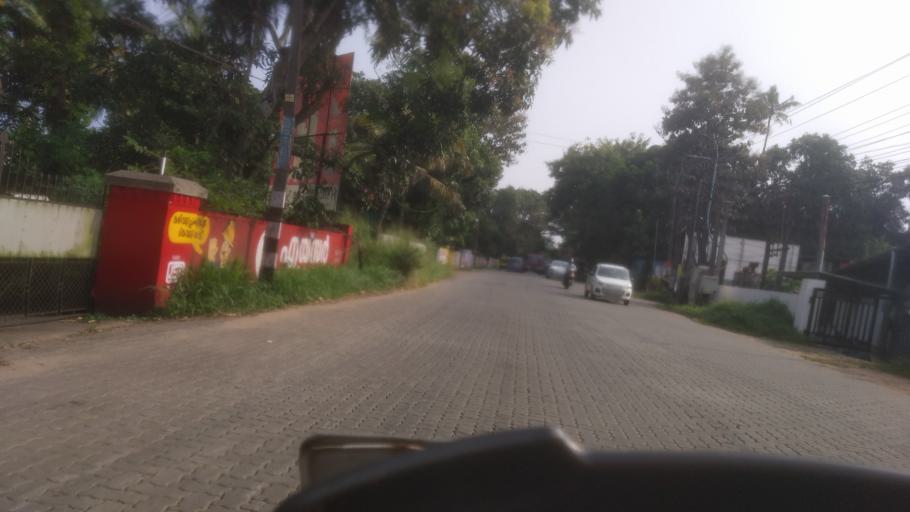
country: IN
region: Kerala
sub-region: Alappuzha
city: Arukutti
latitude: 9.9026
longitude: 76.3682
